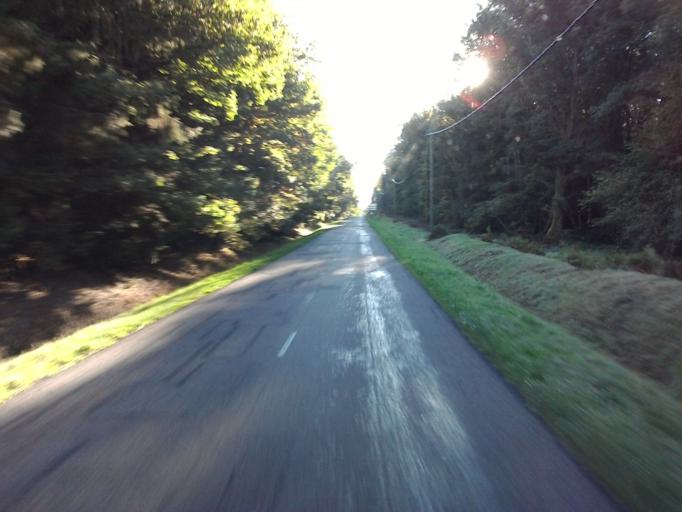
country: FR
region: Bourgogne
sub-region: Departement de la Cote-d'Or
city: Saulieu
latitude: 47.2892
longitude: 4.1665
